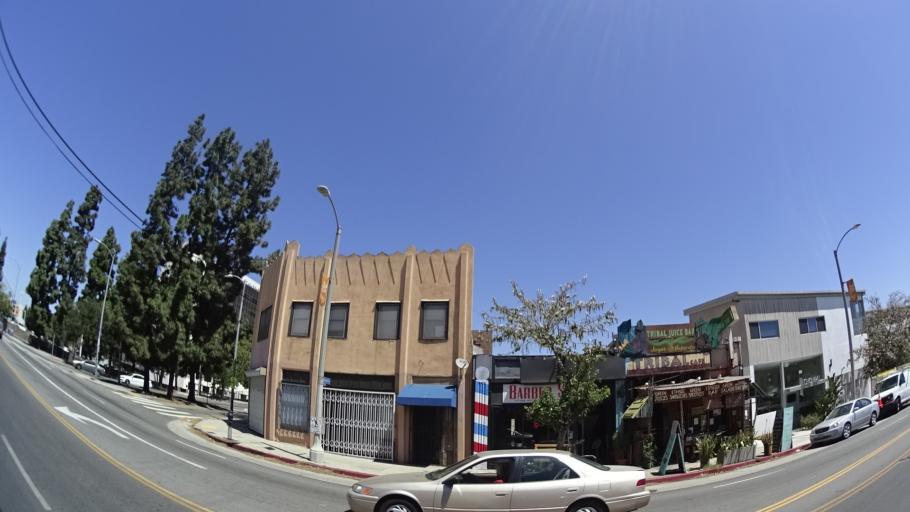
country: US
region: California
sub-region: Los Angeles County
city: Echo Park
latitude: 34.0687
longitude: -118.2628
